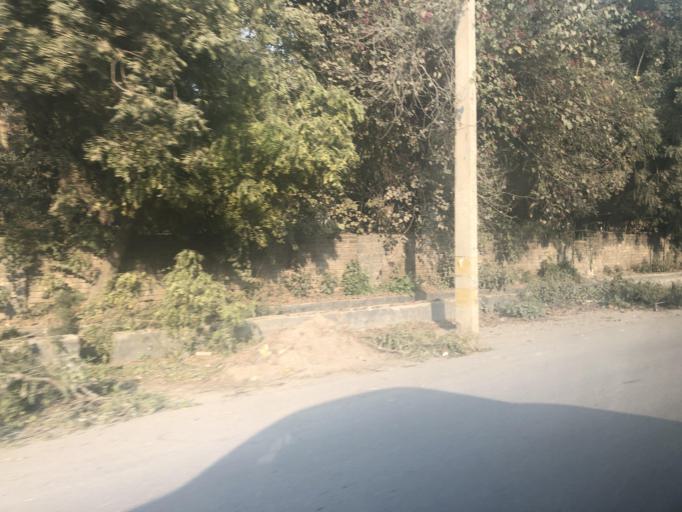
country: IN
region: Haryana
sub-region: Gurgaon
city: Gurgaon
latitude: 28.5397
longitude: 77.0281
